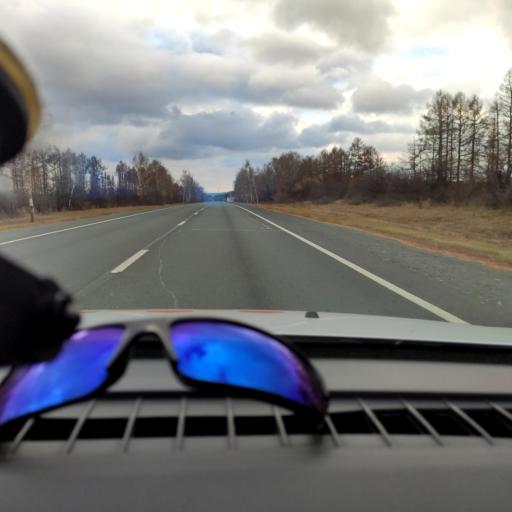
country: RU
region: Samara
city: Volzhskiy
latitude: 53.4631
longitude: 50.1276
